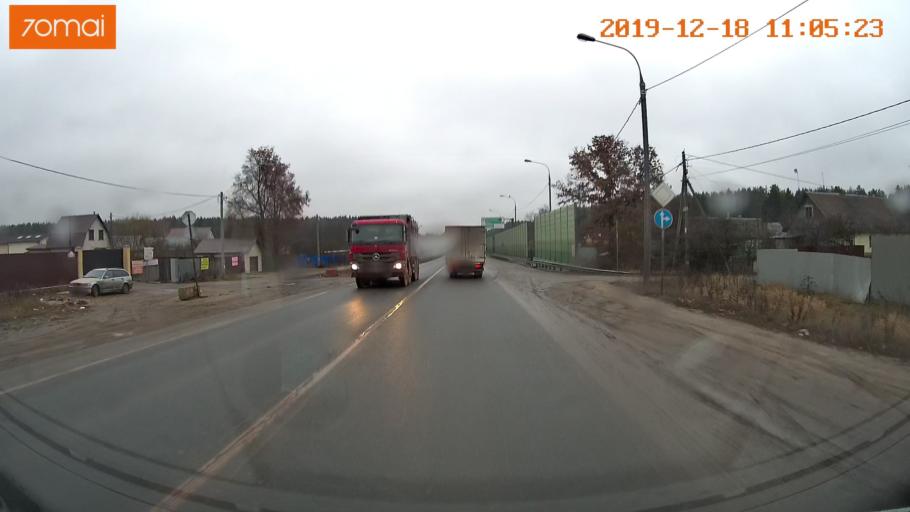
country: RU
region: Moskovskaya
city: Golitsyno
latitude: 55.5975
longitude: 37.0080
